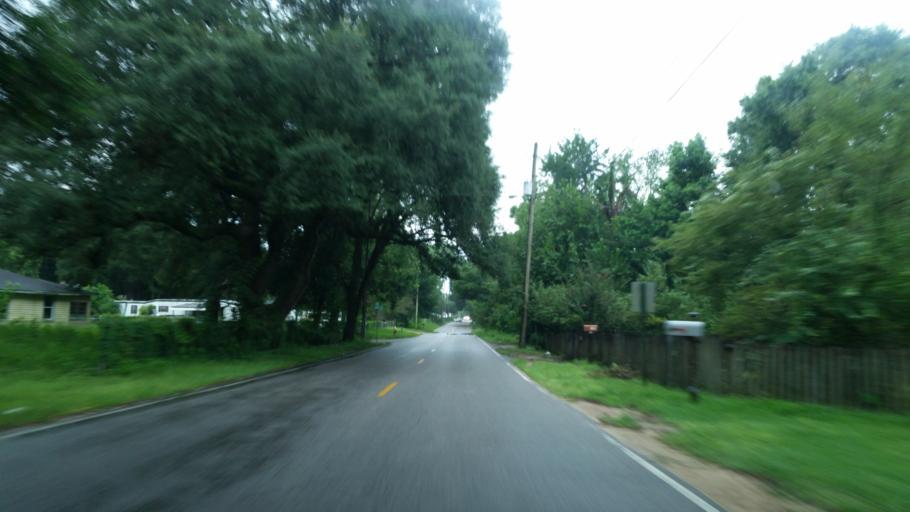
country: US
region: Florida
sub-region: Escambia County
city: West Pensacola
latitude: 30.4265
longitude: -87.2616
